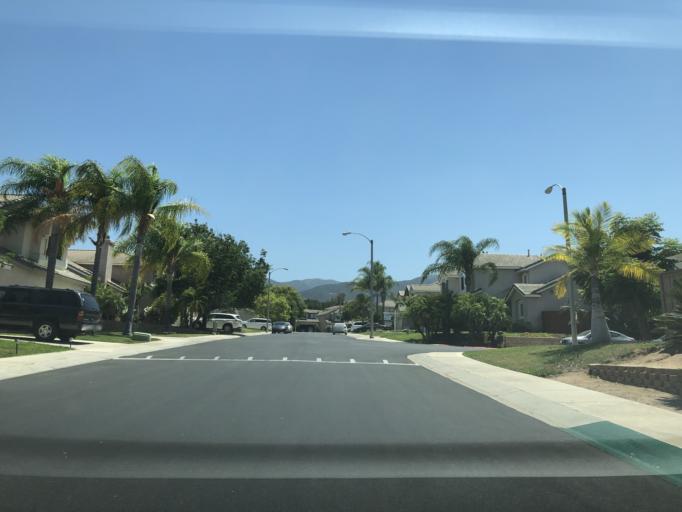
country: US
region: California
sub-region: Riverside County
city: Corona
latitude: 33.8525
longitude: -117.5821
